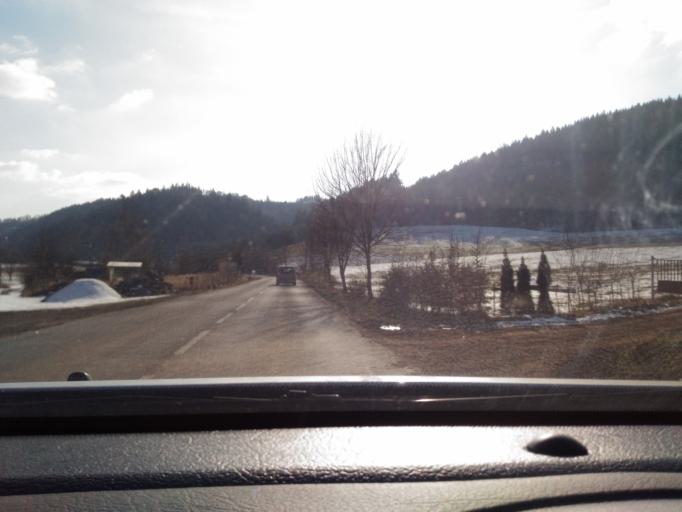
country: CZ
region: South Moravian
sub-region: Okres Brno-Venkov
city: Nedvedice
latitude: 49.4407
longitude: 16.3449
